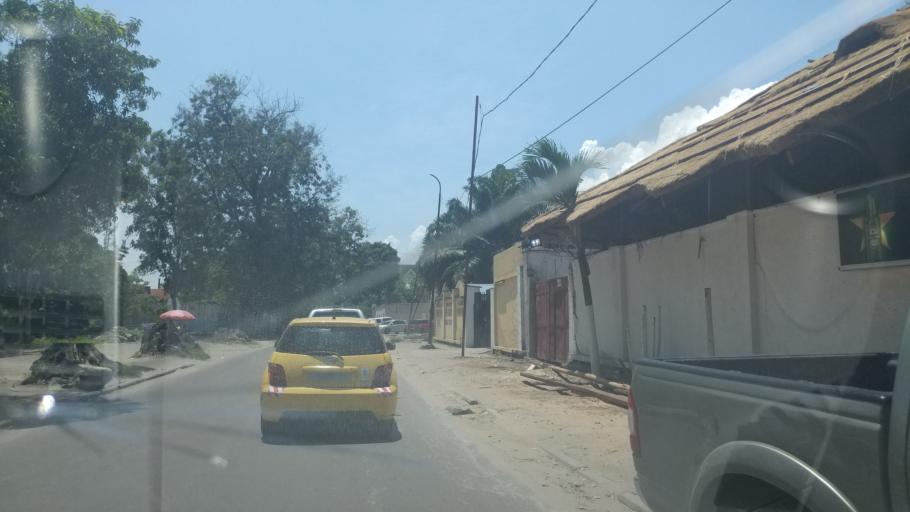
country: CD
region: Kinshasa
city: Kinshasa
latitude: -4.3191
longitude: 15.2807
